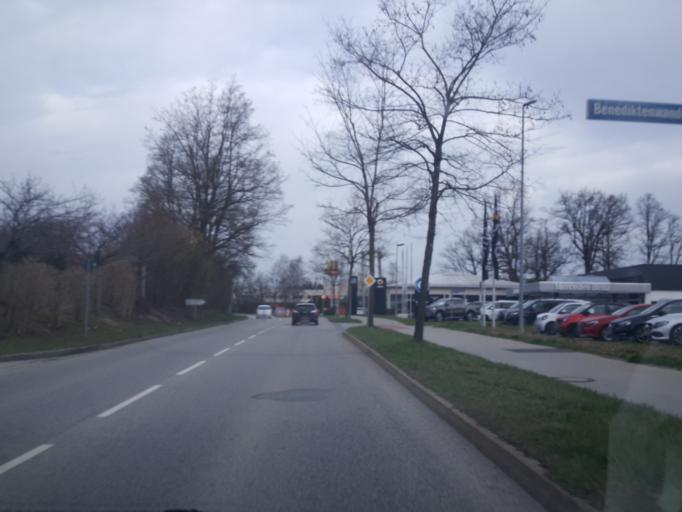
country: DE
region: Bavaria
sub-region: Upper Bavaria
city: Penzberg
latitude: 47.7649
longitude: 11.3607
